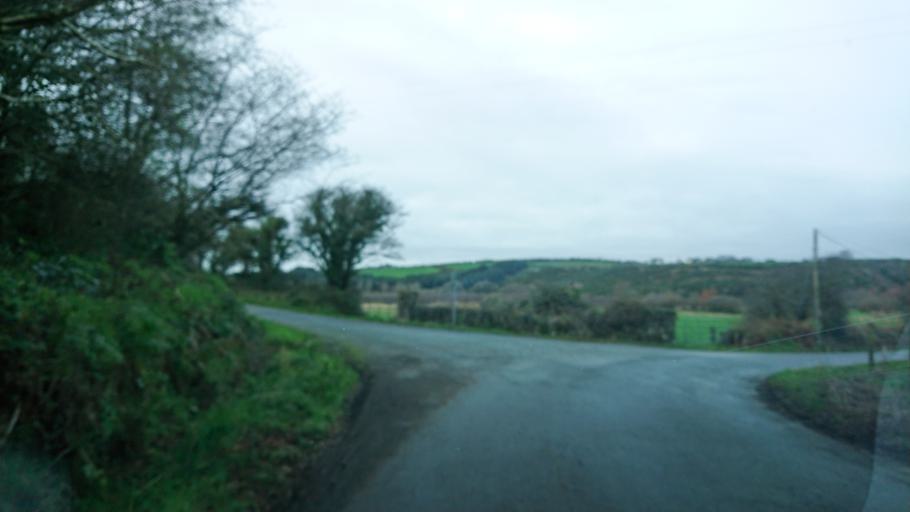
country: IE
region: Munster
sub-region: Waterford
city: Tra Mhor
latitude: 52.1541
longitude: -7.2606
